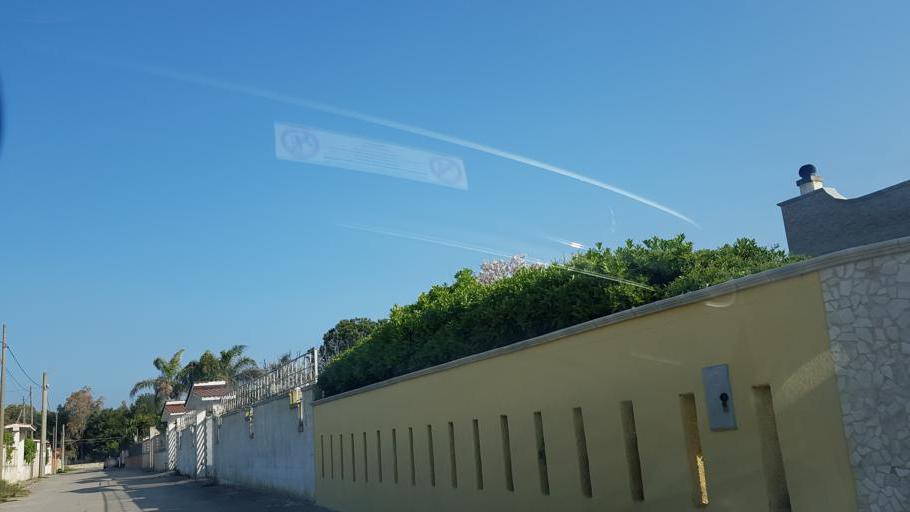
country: IT
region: Apulia
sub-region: Provincia di Brindisi
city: Materdomini
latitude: 40.6676
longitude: 17.9427
